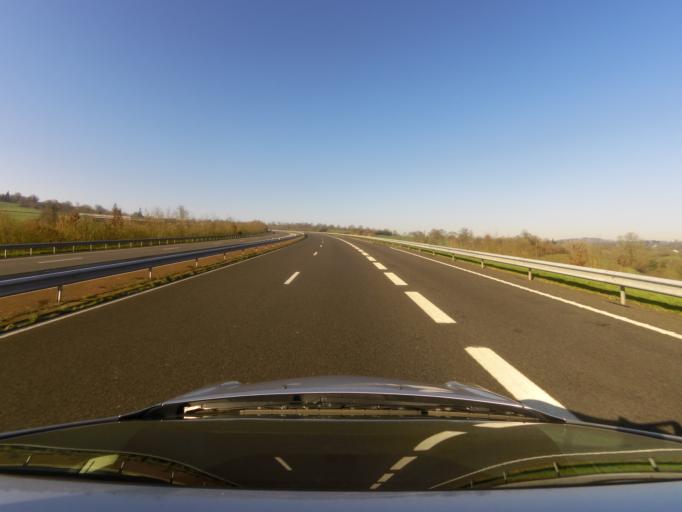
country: FR
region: Lower Normandy
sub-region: Departement de la Manche
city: Tessy-sur-Vire
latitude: 48.9380
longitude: -1.0667
